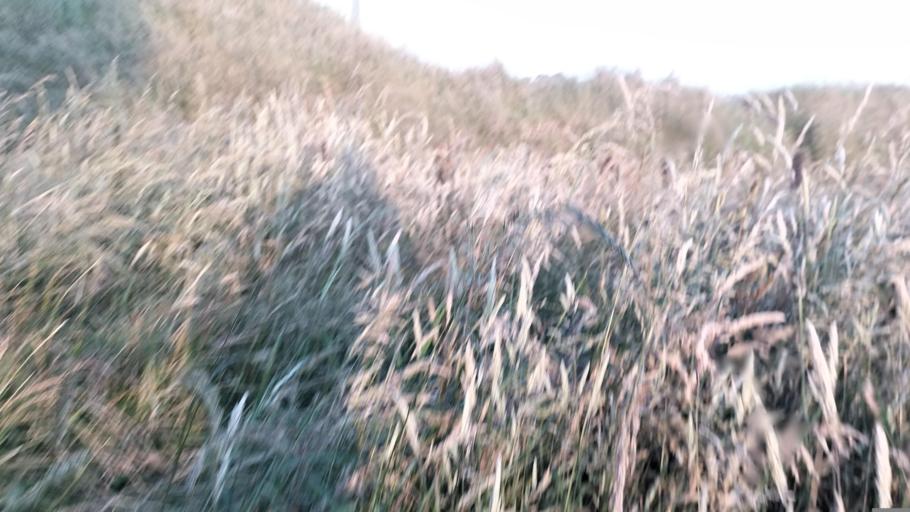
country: NZ
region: Auckland
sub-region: Auckland
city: Auckland
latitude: -36.9009
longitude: 174.7814
